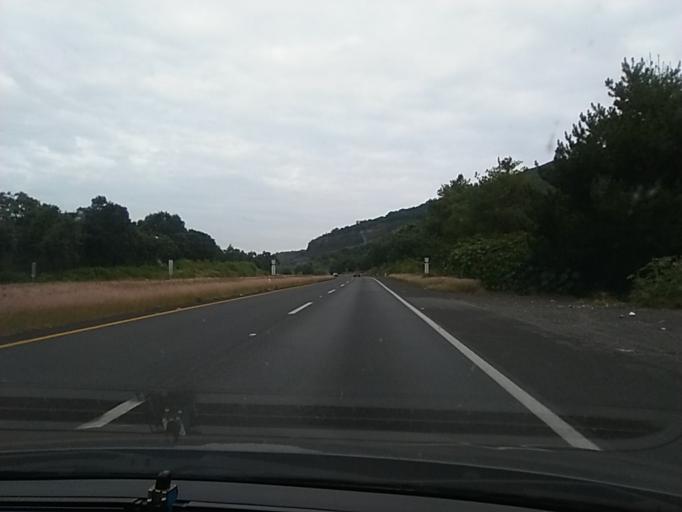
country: MX
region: Michoacan
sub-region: Puruandiro
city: San Lorenzo
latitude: 19.9618
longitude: -101.6911
